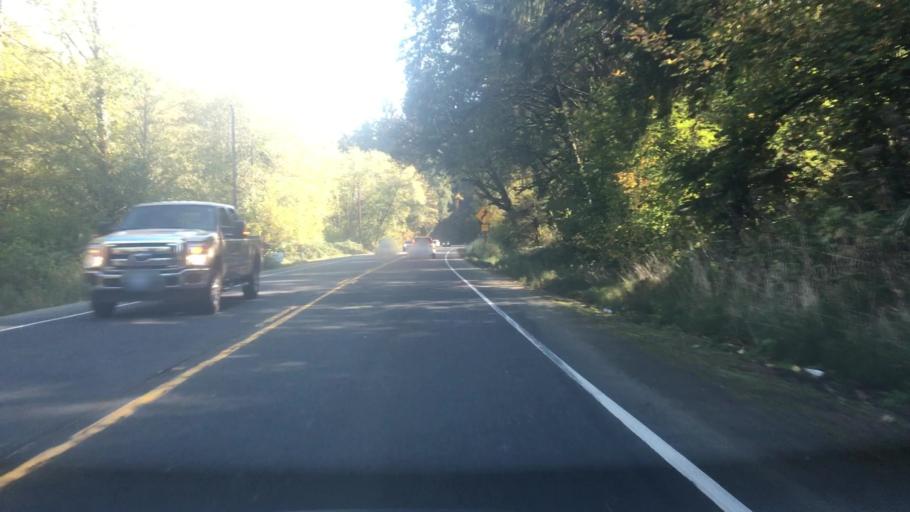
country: US
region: Oregon
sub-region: Lincoln County
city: Rose Lodge
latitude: 45.0098
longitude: -123.9221
